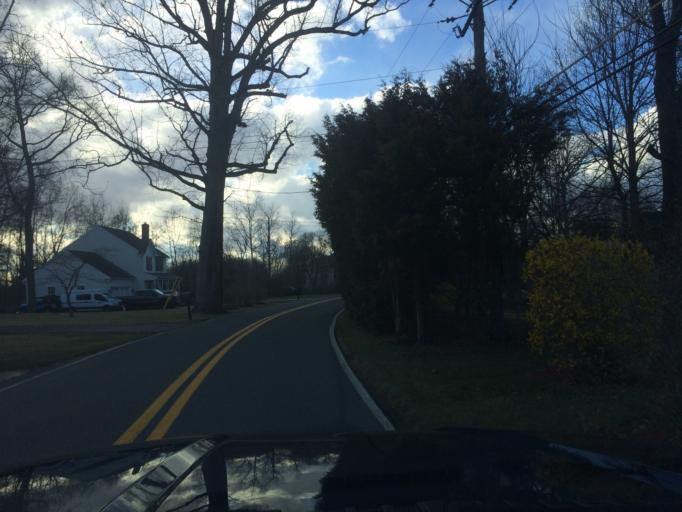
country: US
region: Maryland
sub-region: Carroll County
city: Eldersburg
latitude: 39.3779
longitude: -76.9083
